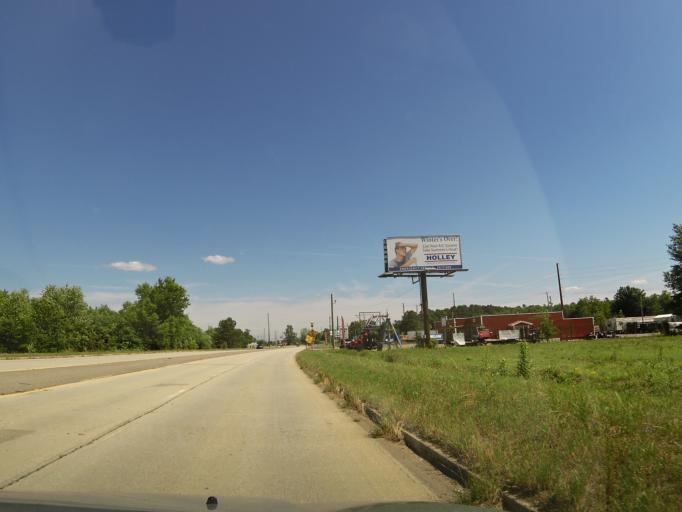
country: US
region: South Carolina
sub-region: Aiken County
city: Aiken
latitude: 33.5493
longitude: -81.6868
